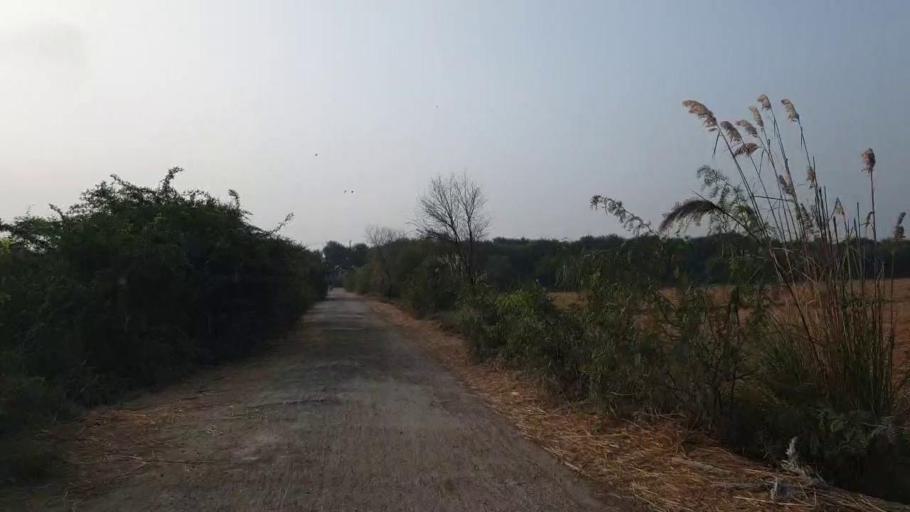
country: PK
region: Sindh
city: Tando Muhammad Khan
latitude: 25.1378
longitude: 68.6038
